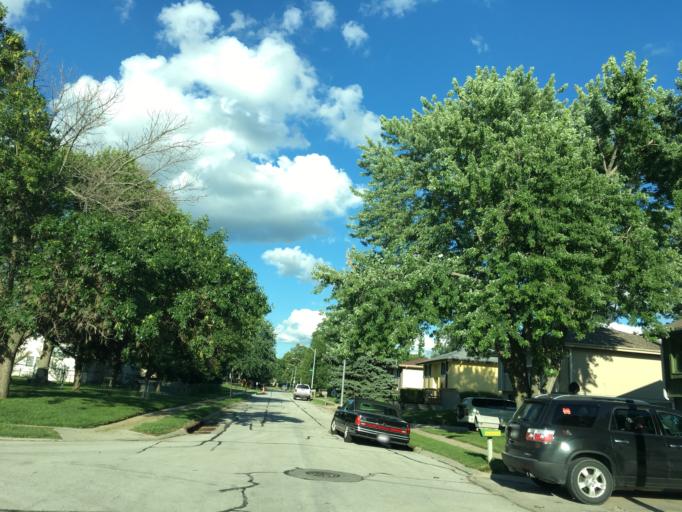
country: US
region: Nebraska
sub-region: Sarpy County
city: La Vista
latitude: 41.1743
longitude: -95.9912
